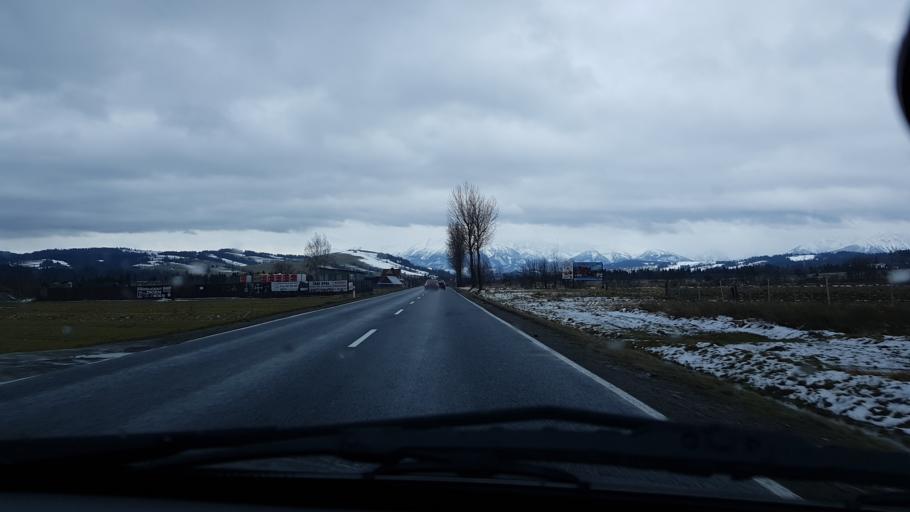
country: PL
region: Lesser Poland Voivodeship
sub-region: Powiat tatrzanski
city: Bialka Tatrzanska
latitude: 49.4139
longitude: 20.0975
